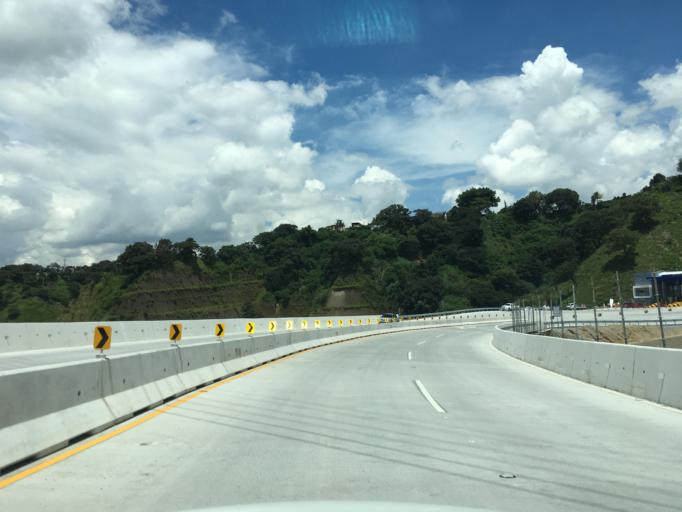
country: GT
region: Guatemala
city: Petapa
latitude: 14.5363
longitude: -90.5358
